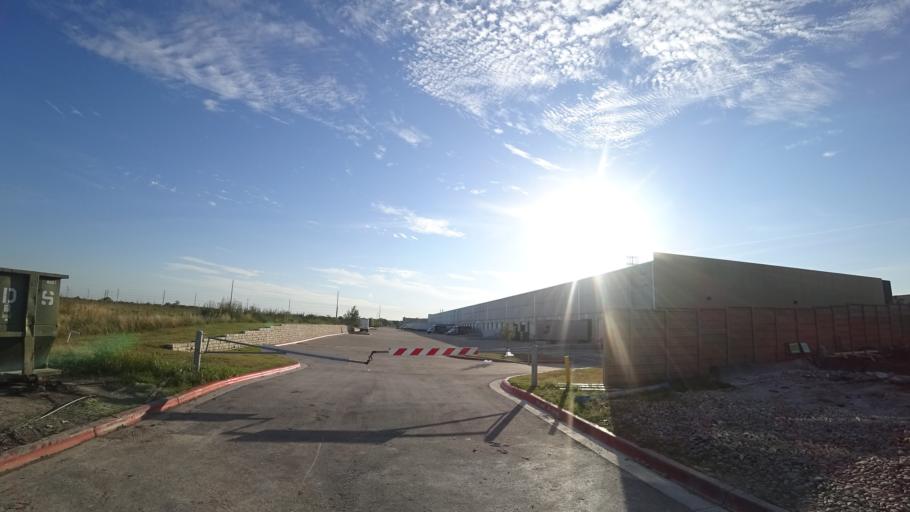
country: US
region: Texas
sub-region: Travis County
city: Pflugerville
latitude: 30.4128
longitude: -97.6434
